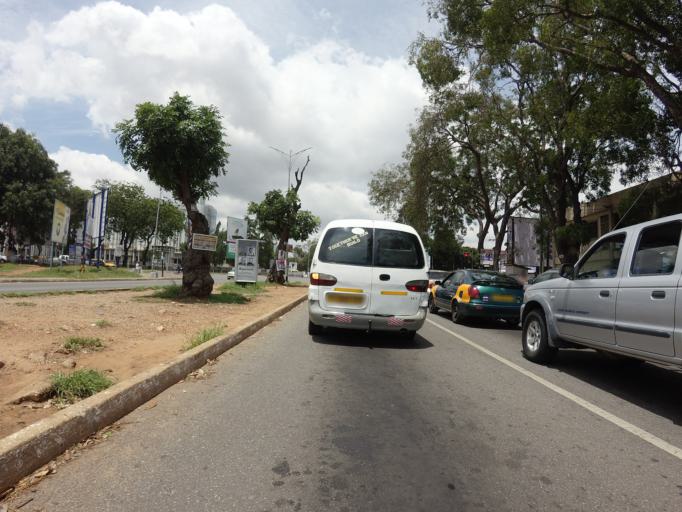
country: GH
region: Greater Accra
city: Accra
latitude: 5.5616
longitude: -0.2060
